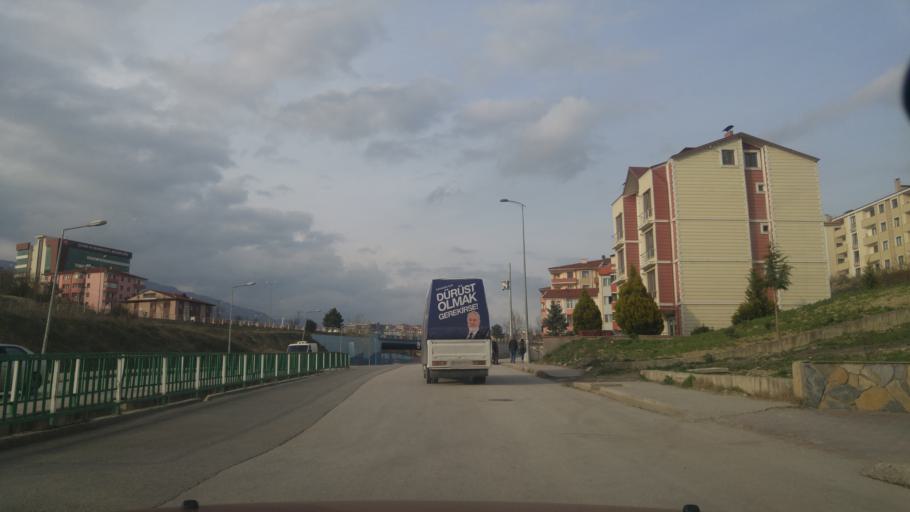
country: TR
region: Karabuk
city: Karabuk
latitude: 41.2232
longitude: 32.6628
